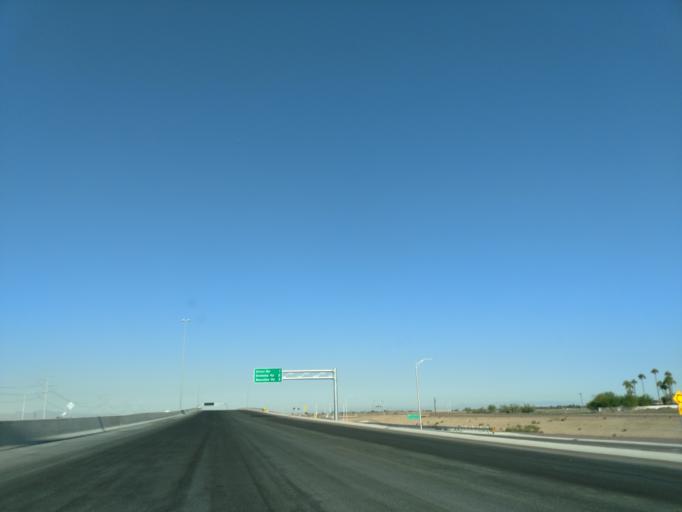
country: US
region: Arizona
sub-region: Maricopa County
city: Laveen
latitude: 33.3311
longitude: -112.1734
